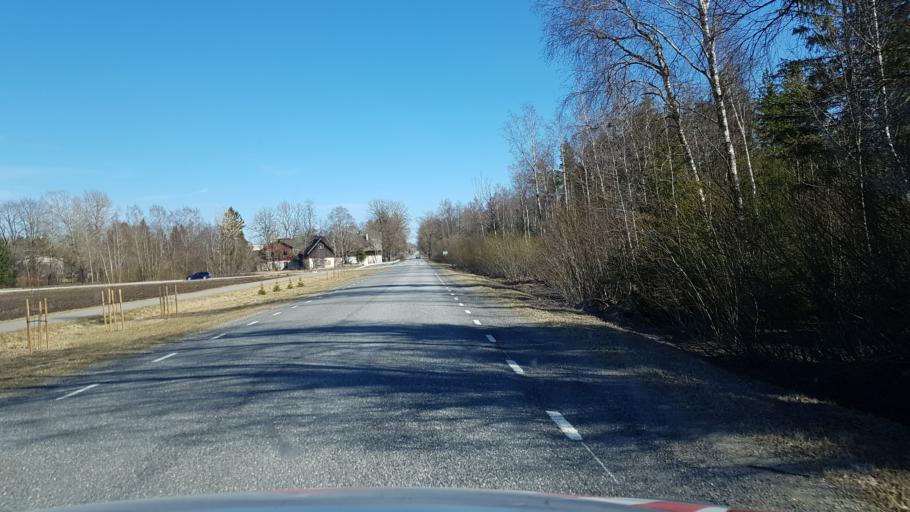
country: EE
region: Laeaene-Virumaa
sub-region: Rakke vald
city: Rakke
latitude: 58.9932
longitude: 26.2243
